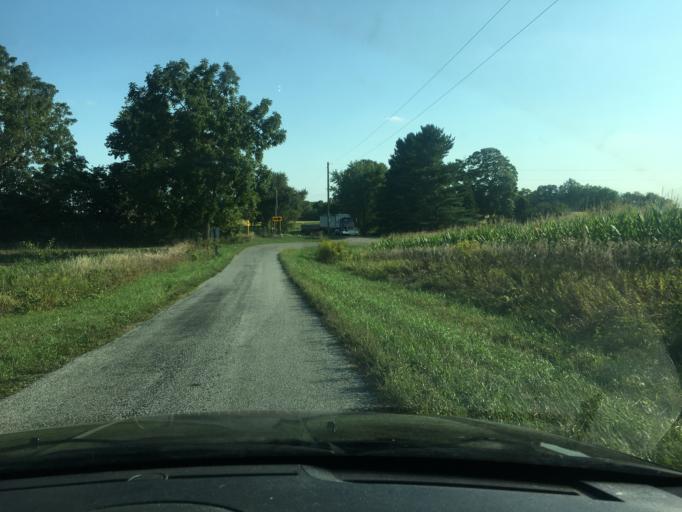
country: US
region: Ohio
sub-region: Logan County
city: West Liberty
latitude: 40.2313
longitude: -83.7869
